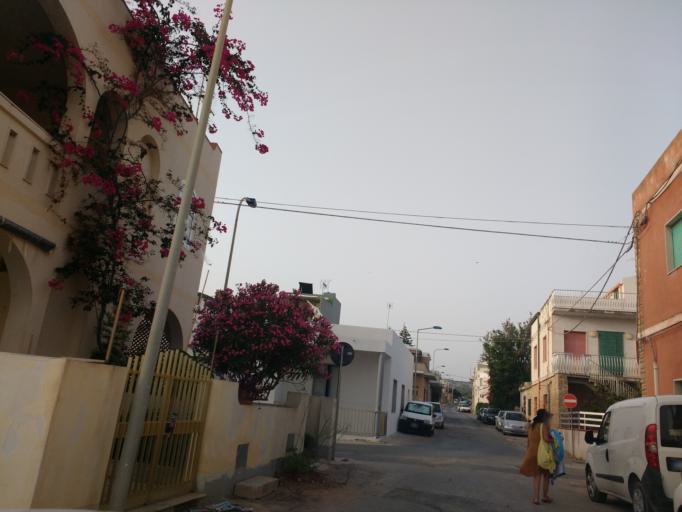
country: IT
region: Sicily
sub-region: Ragusa
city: Cava d'Aliga
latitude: 36.7298
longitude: 14.6857
